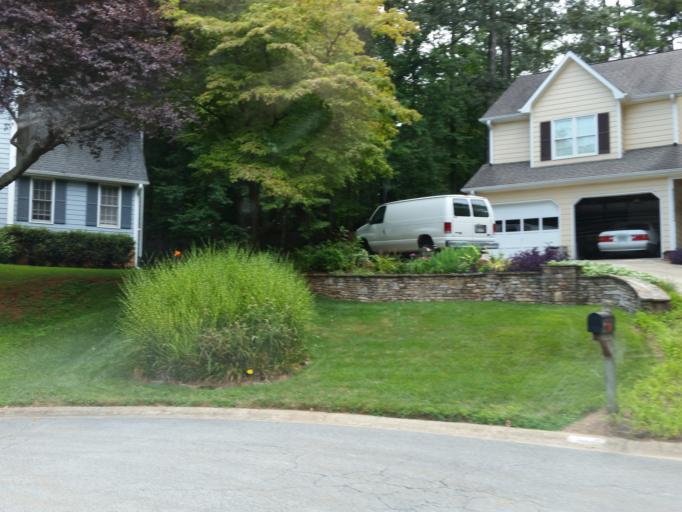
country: US
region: Georgia
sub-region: Cherokee County
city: Woodstock
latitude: 34.0507
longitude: -84.5100
